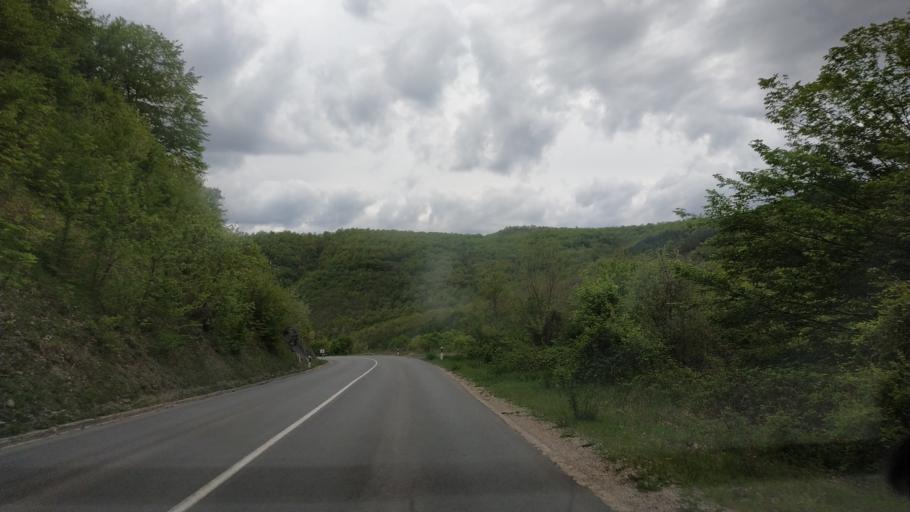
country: RS
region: Central Serbia
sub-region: Zajecarski Okrug
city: Soko Banja
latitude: 43.6527
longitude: 21.7536
